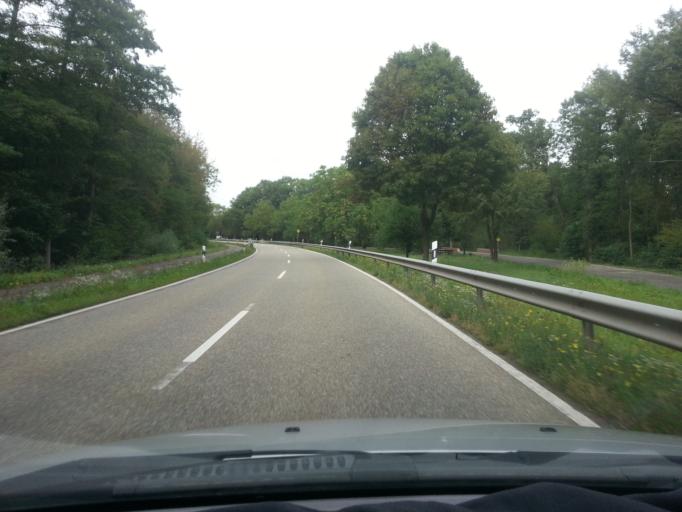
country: DE
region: Rheinland-Pfalz
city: Offenbach an der Queich
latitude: 49.2109
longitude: 8.1895
